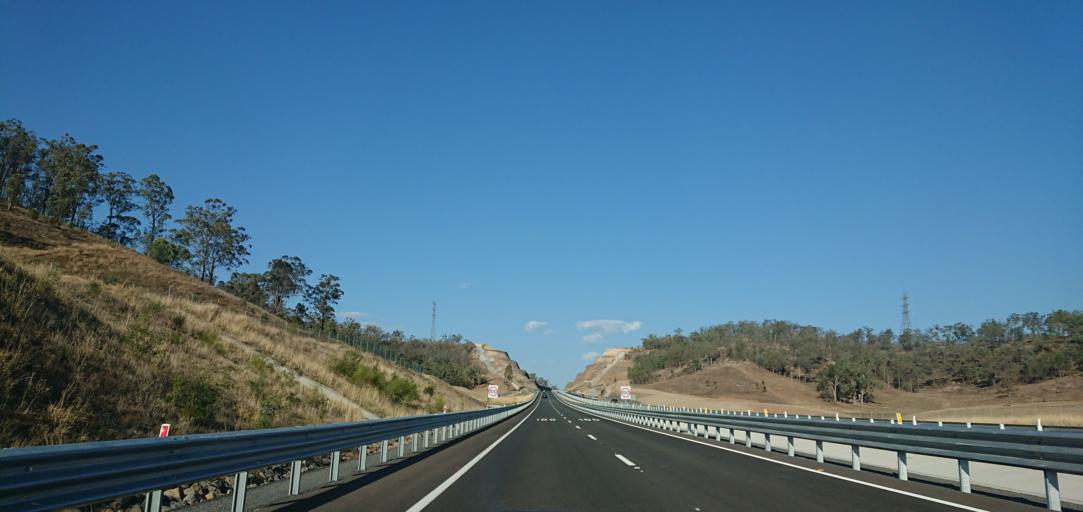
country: AU
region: Queensland
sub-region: Toowoomba
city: East Toowoomba
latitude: -27.5151
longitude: 152.0325
